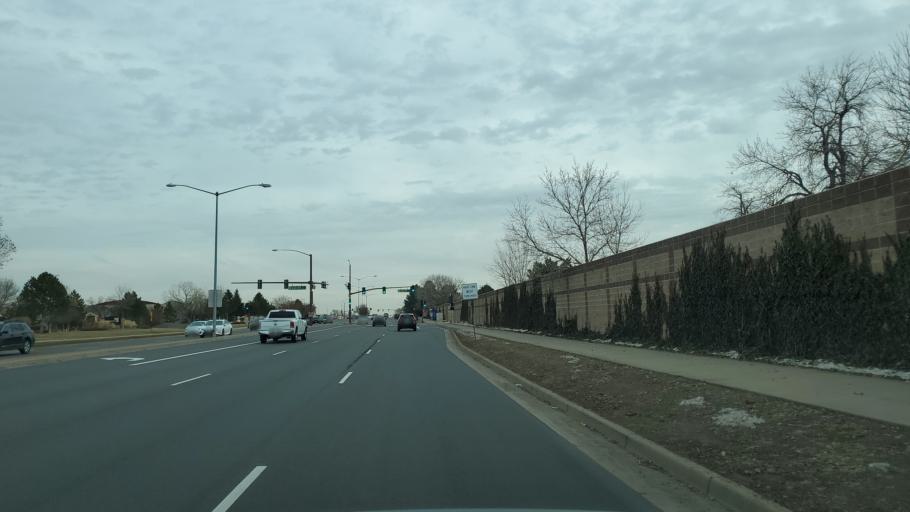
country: US
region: Colorado
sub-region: Adams County
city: Northglenn
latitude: 39.9137
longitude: -104.9471
